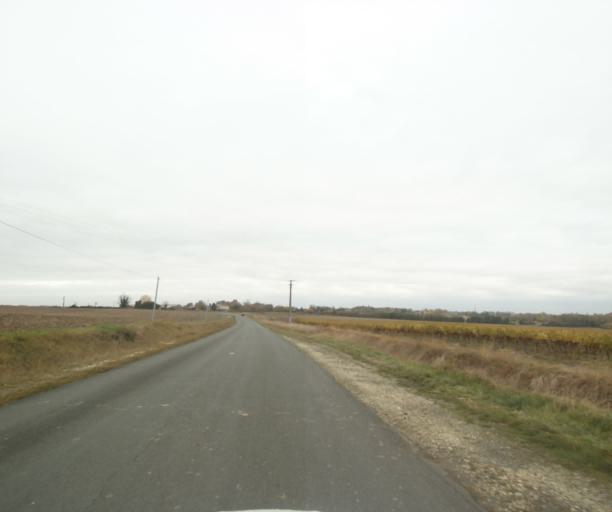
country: FR
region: Poitou-Charentes
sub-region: Departement de la Charente-Maritime
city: Saintes
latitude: 45.7301
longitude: -0.6641
